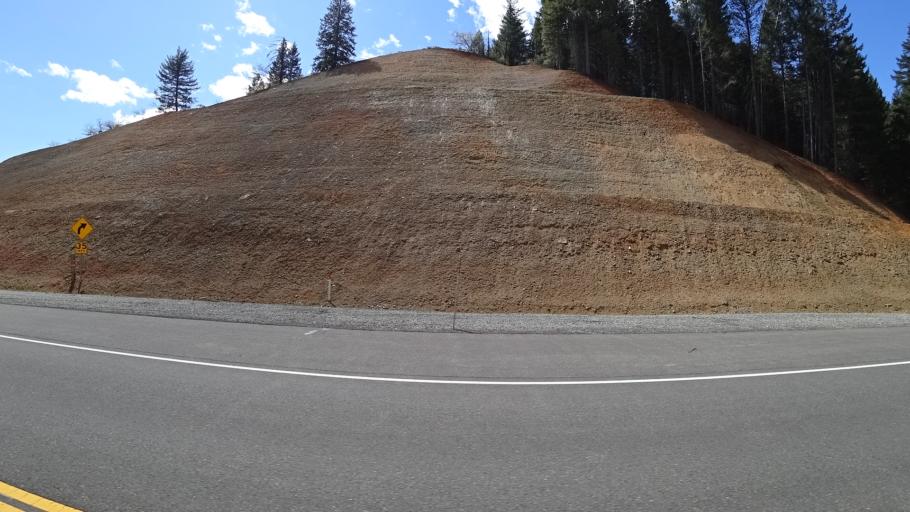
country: US
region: California
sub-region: Trinity County
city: Weaverville
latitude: 40.8241
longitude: -122.8881
